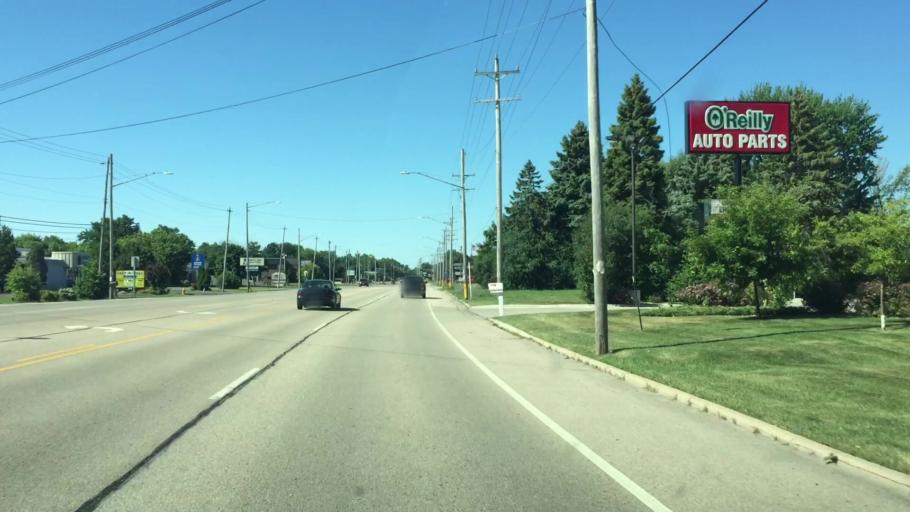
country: US
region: Wisconsin
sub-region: Winnebago County
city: Menasha
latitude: 44.2256
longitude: -88.4249
